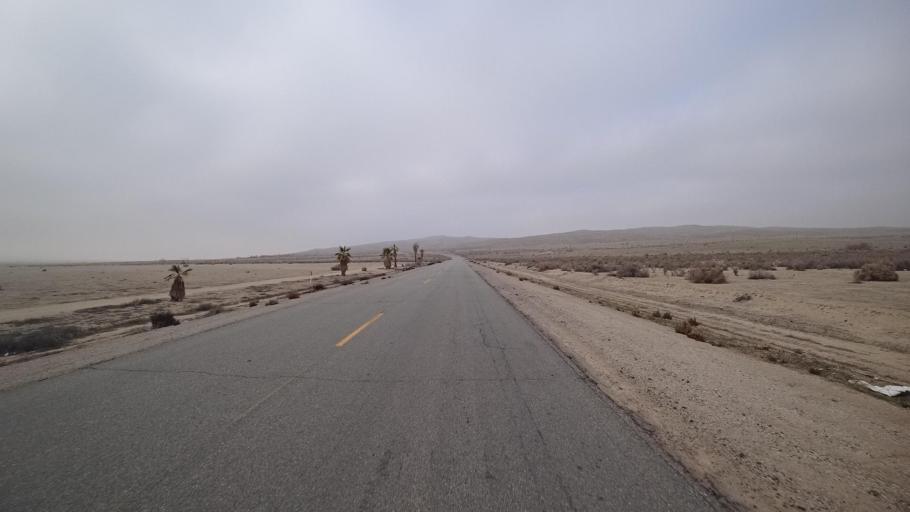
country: US
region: California
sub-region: Kern County
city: Maricopa
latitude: 35.1252
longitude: -119.3631
